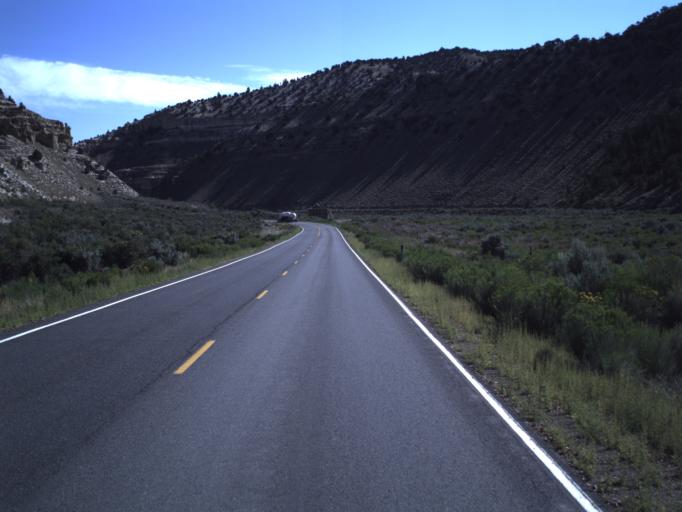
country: US
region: Utah
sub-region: Duchesne County
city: Duchesne
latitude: 40.0343
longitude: -110.5411
